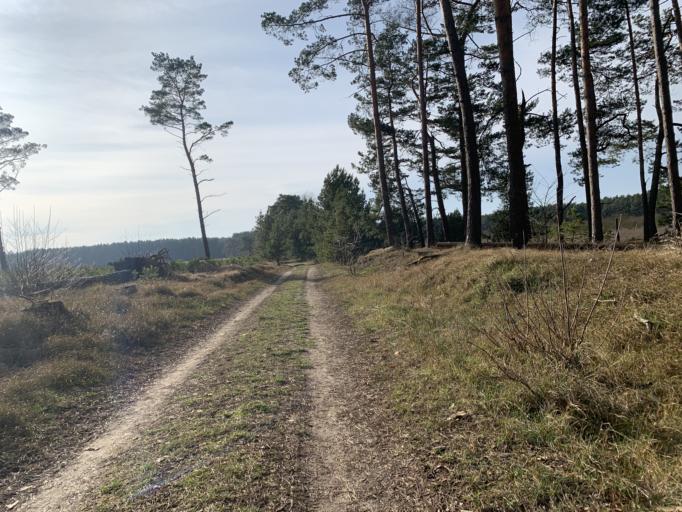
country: DE
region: Mecklenburg-Vorpommern
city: Wesenberg
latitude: 53.2908
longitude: 12.8693
